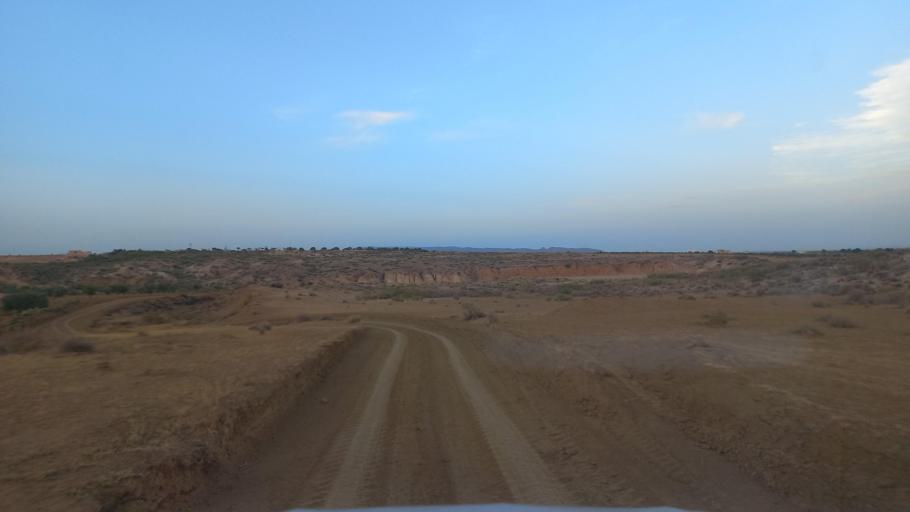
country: TN
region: Al Qasrayn
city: Kasserine
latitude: 35.2028
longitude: 9.0542
